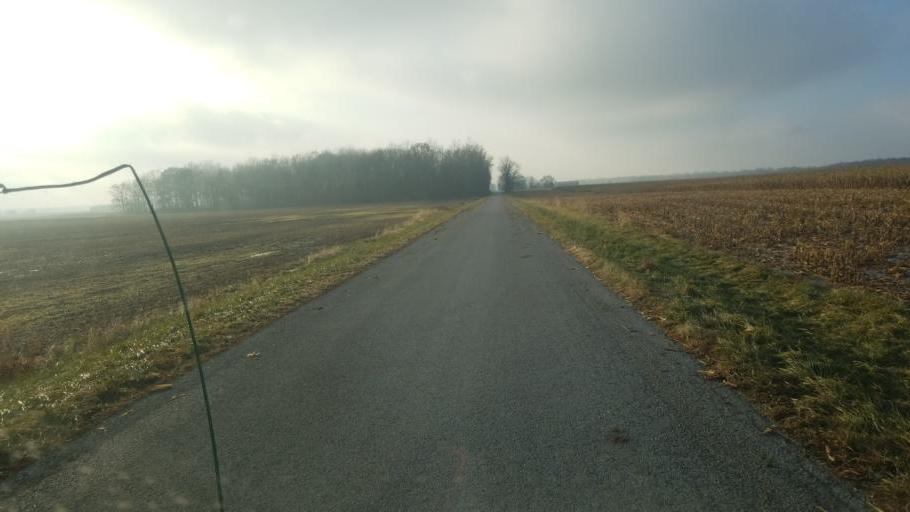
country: US
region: Ohio
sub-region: Hardin County
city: Kenton
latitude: 40.6882
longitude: -83.5766
